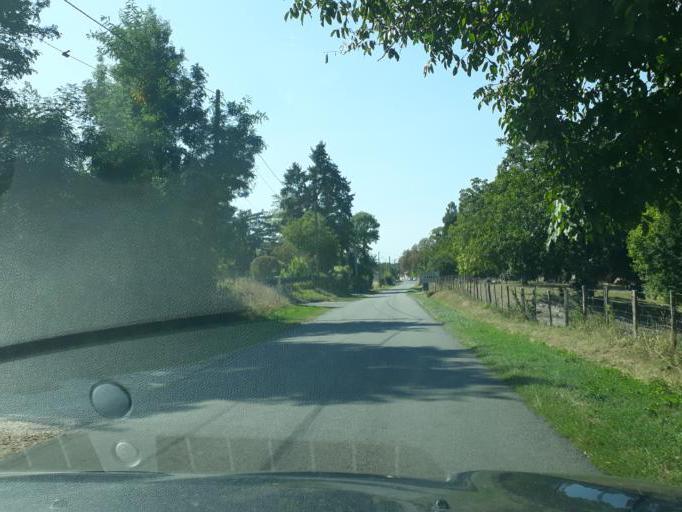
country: FR
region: Centre
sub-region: Departement de l'Indre
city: Chabris
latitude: 47.2562
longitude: 1.6706
